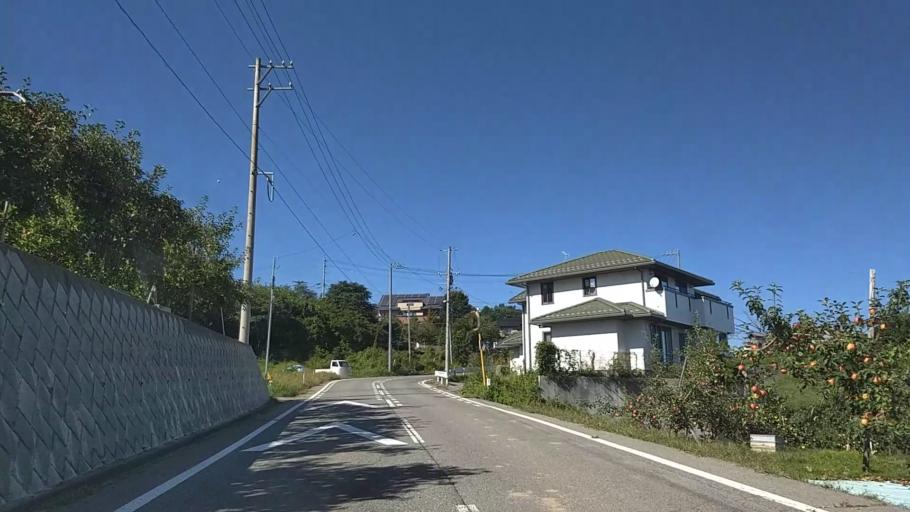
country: JP
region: Nagano
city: Nagano-shi
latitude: 36.5838
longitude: 138.1114
